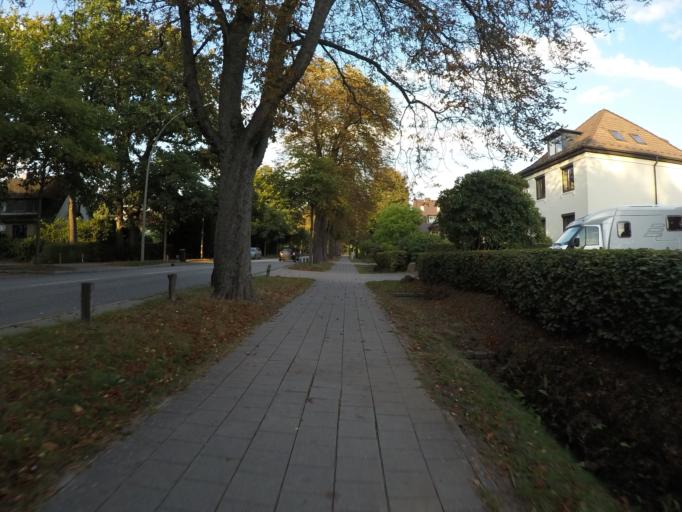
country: DE
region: Hamburg
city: Sasel
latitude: 53.6358
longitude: 10.1493
